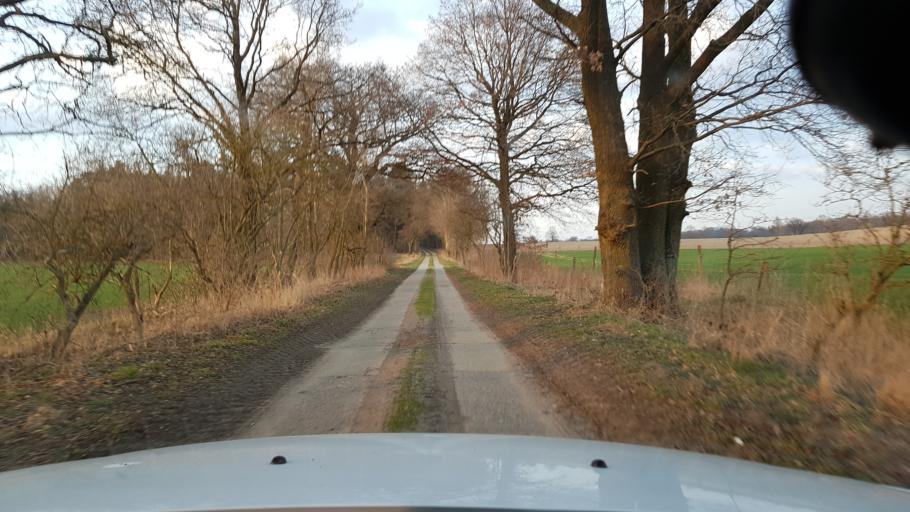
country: PL
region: West Pomeranian Voivodeship
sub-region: Koszalin
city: Koszalin
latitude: 54.1000
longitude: 16.1443
